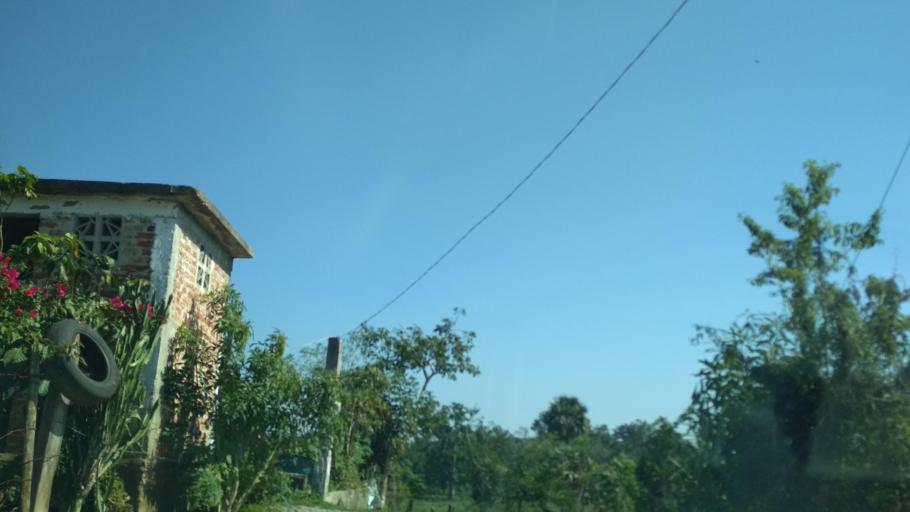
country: MX
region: Veracruz
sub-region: Papantla
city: El Chote
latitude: 20.3992
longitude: -97.3315
